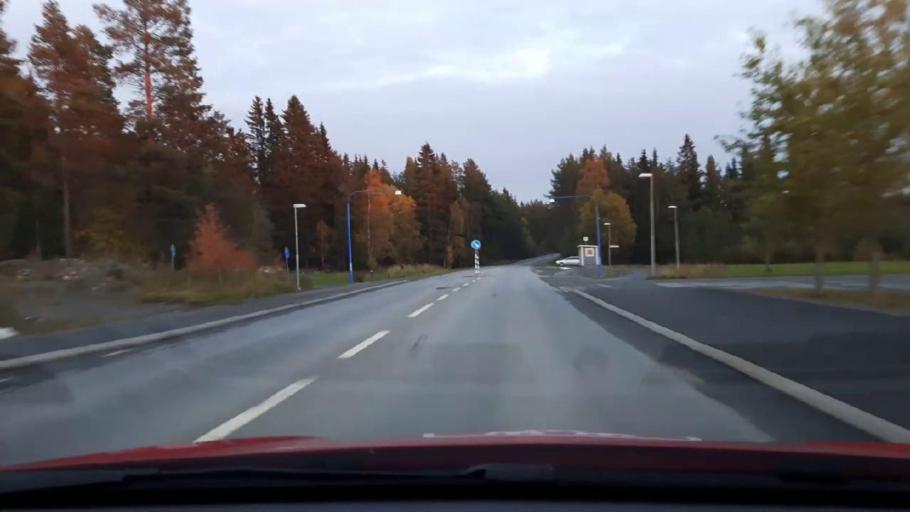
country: SE
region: Jaemtland
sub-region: OEstersunds Kommun
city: Ostersund
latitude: 63.2151
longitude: 14.6193
